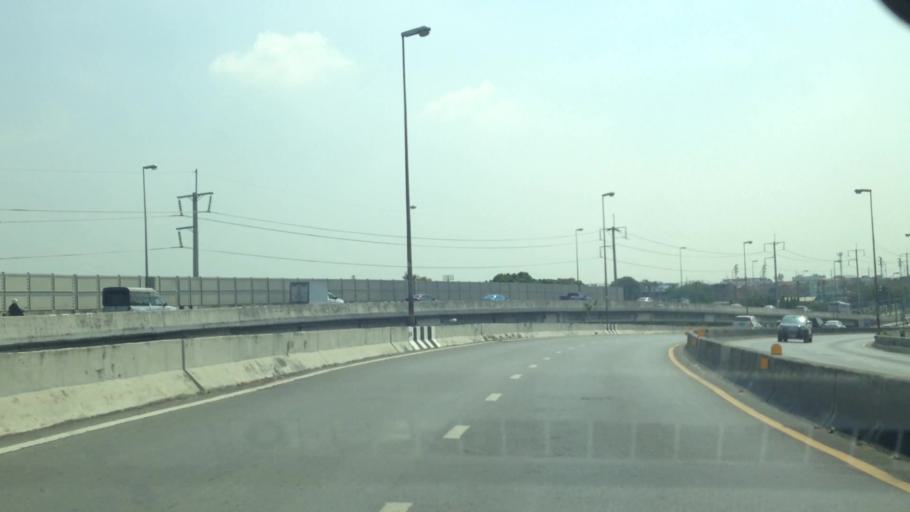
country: TH
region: Bangkok
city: Sai Mai
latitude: 13.9554
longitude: 100.6211
